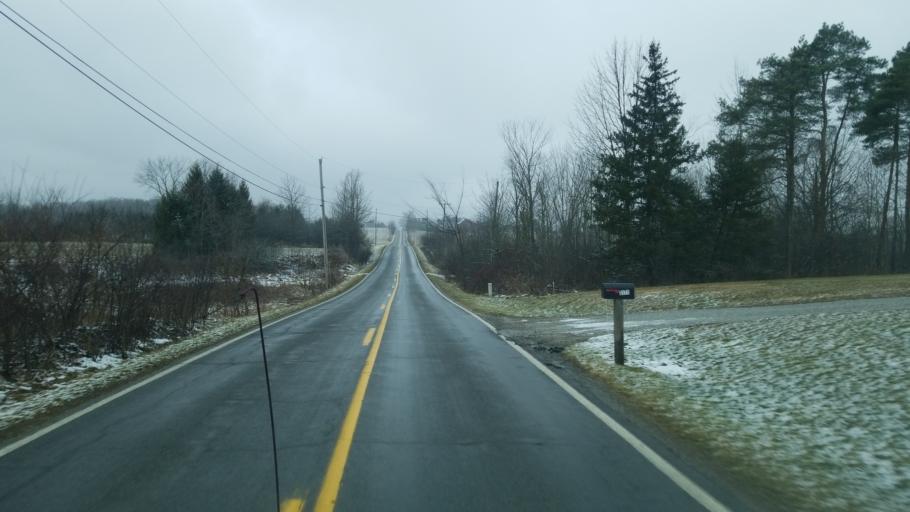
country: US
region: Ohio
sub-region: Portage County
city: Mantua
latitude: 41.2841
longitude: -81.2780
